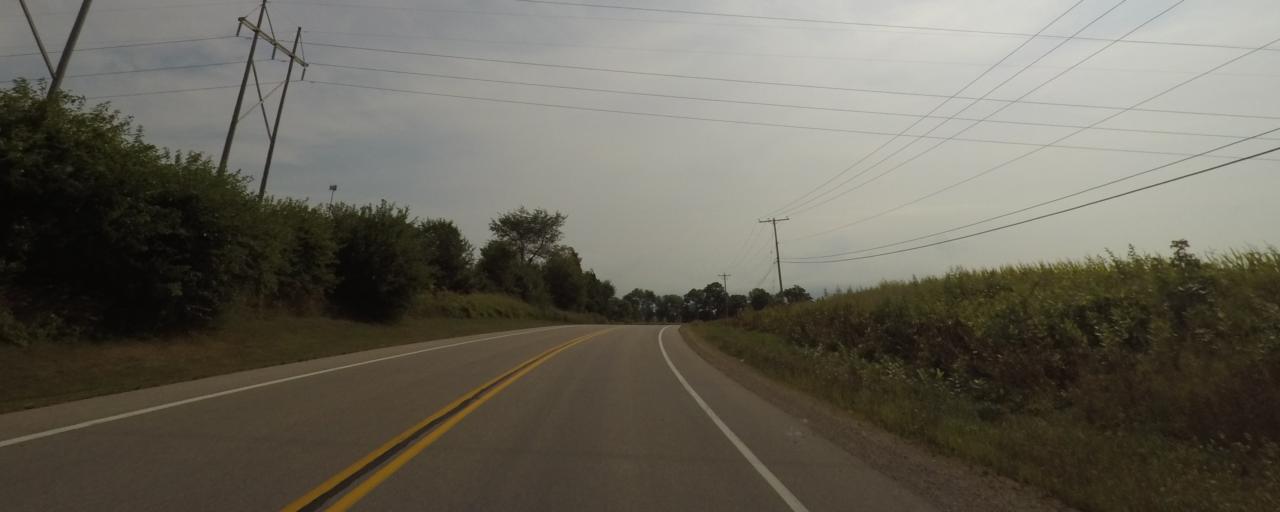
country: US
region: Wisconsin
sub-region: Jefferson County
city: Jefferson
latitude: 42.9854
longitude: -88.8661
